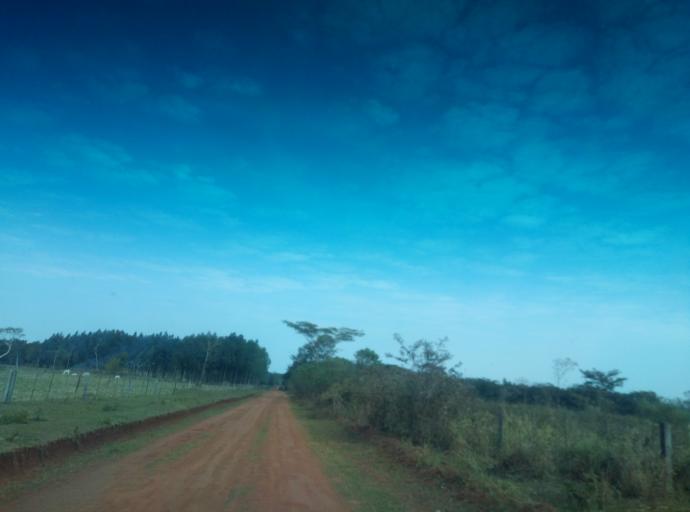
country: PY
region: Caaguazu
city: Carayao
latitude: -25.1928
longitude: -56.2520
